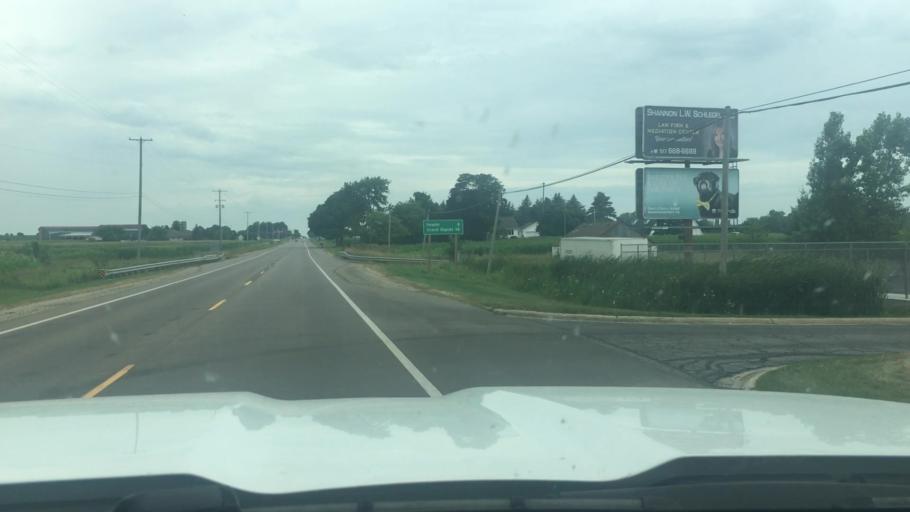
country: US
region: Michigan
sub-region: Clinton County
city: Saint Johns
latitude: 43.0016
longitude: -84.5736
